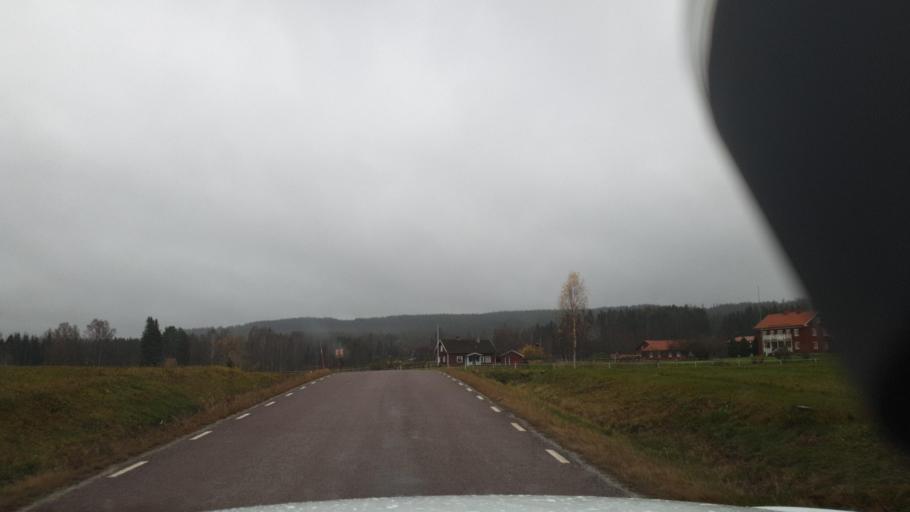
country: SE
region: Vaermland
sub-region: Sunne Kommun
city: Sunne
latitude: 59.7429
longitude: 13.0598
